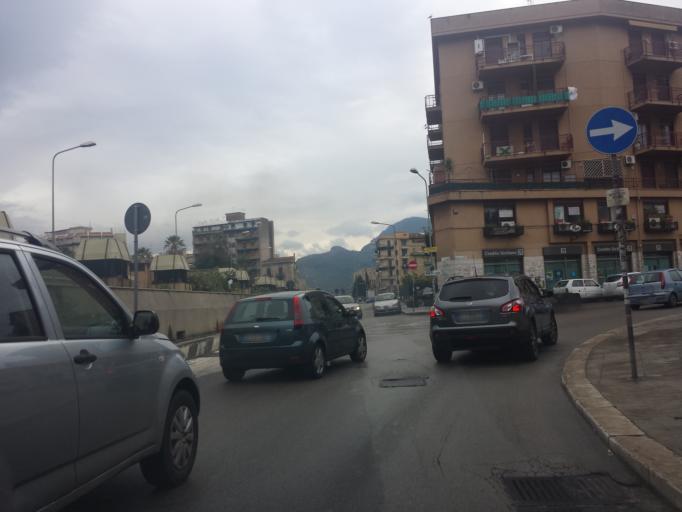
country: IT
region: Sicily
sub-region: Palermo
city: Palermo
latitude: 38.1089
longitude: 13.3540
